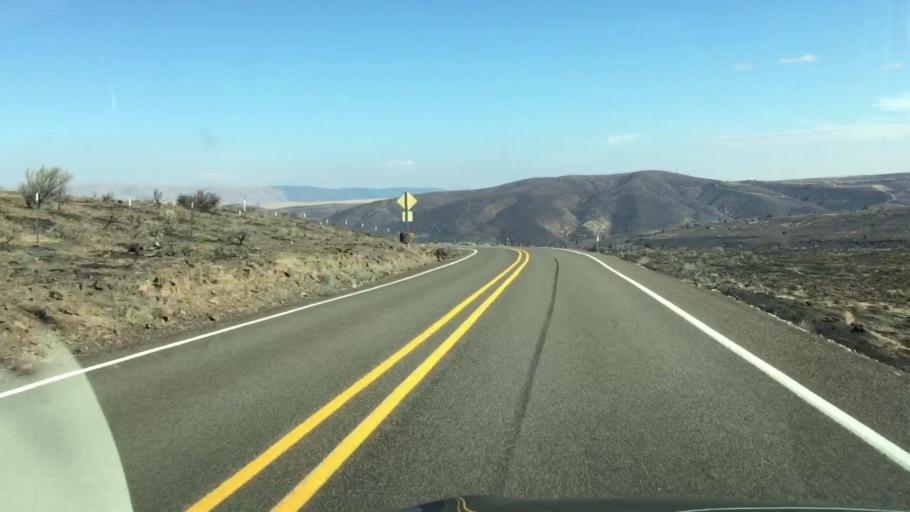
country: US
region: Oregon
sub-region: Jefferson County
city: Warm Springs
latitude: 45.1379
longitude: -121.0517
